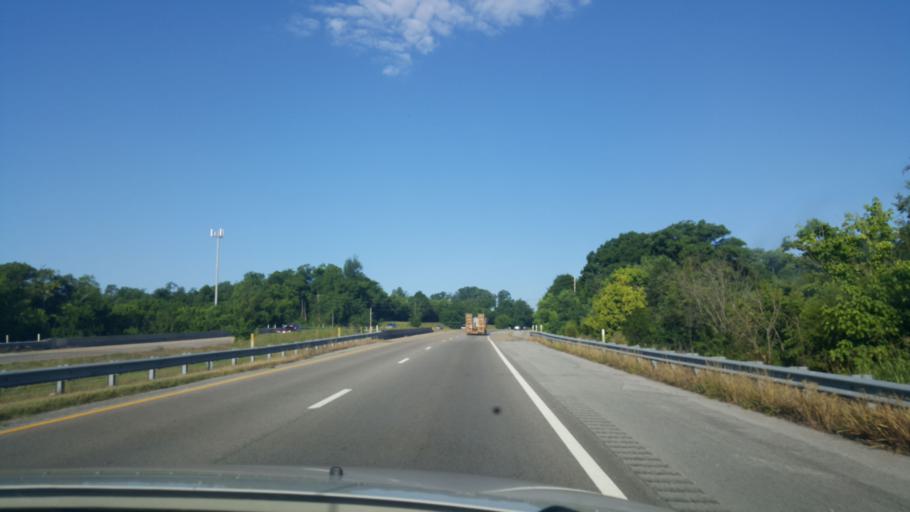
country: US
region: Tennessee
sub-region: Maury County
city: Columbia
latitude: 35.6277
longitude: -87.0734
